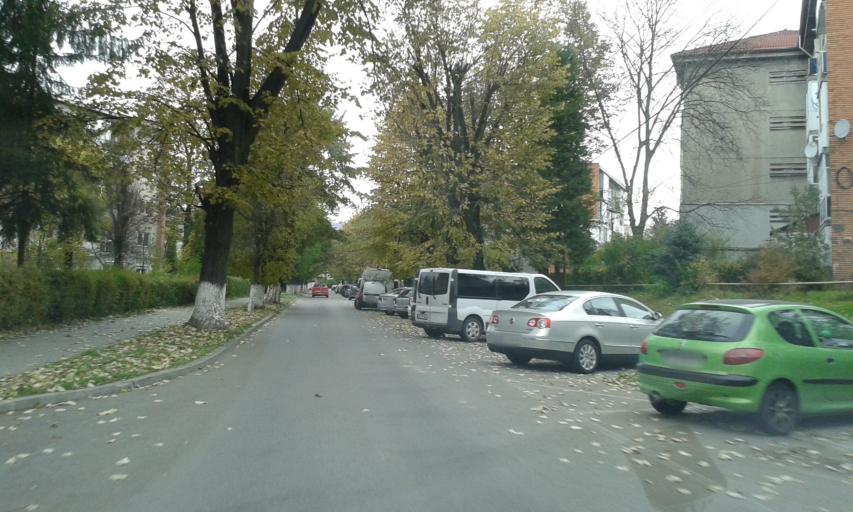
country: RO
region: Hunedoara
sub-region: Municipiul Petrosani
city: Petrosani
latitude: 45.4033
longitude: 23.3767
